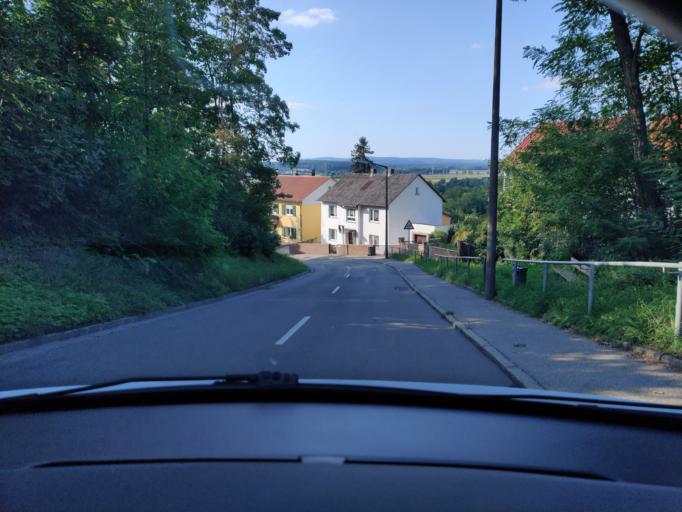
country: DE
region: Bavaria
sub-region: Upper Palatinate
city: Schwandorf in Bayern
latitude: 49.3299
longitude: 12.1106
